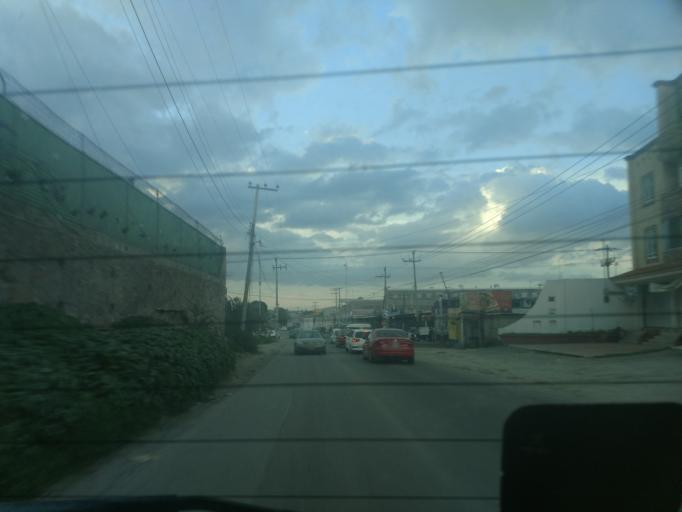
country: MX
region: Mexico
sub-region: Cuautitlan
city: Barrio Tlatenco
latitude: 19.7470
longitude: -99.2000
